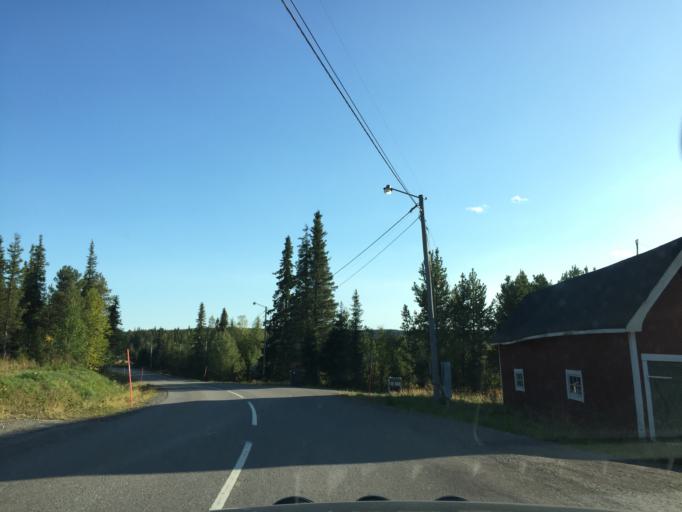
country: SE
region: Norrbotten
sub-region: Gallivare Kommun
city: Malmberget
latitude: 67.6428
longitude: 21.0598
